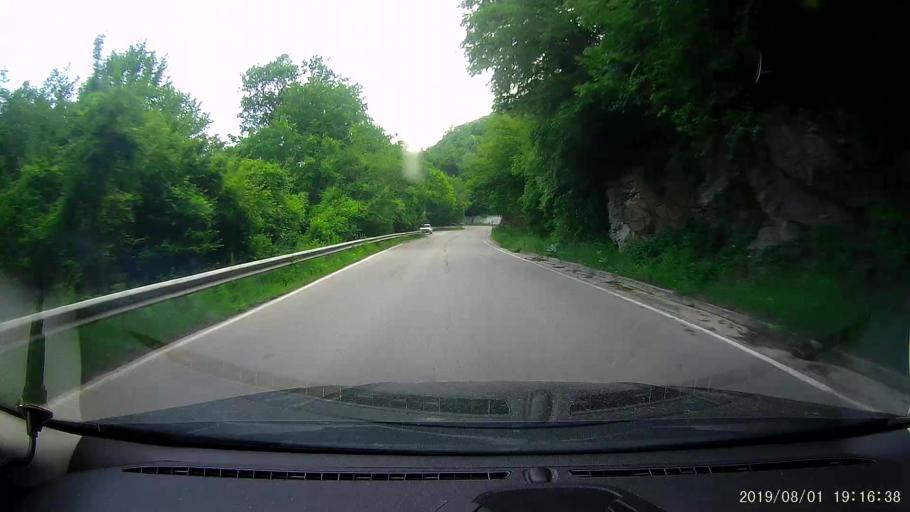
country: BG
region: Shumen
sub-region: Obshtina Smyadovo
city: Smyadovo
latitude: 42.9322
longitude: 26.9505
